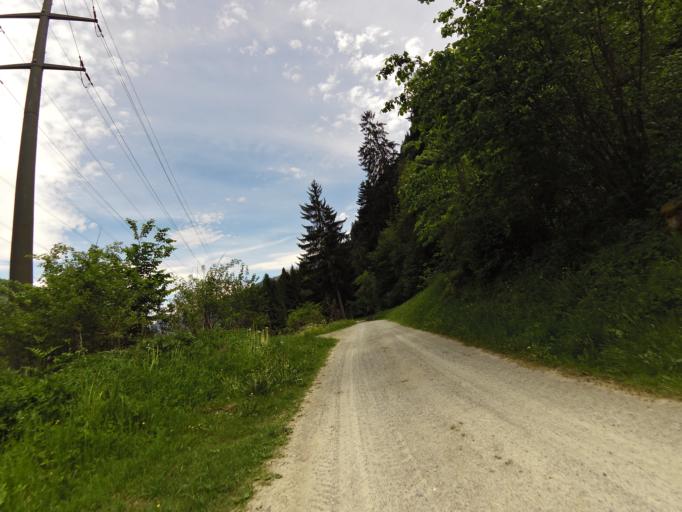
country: CH
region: Grisons
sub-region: Surselva District
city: Ilanz
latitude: 46.7745
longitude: 9.1549
